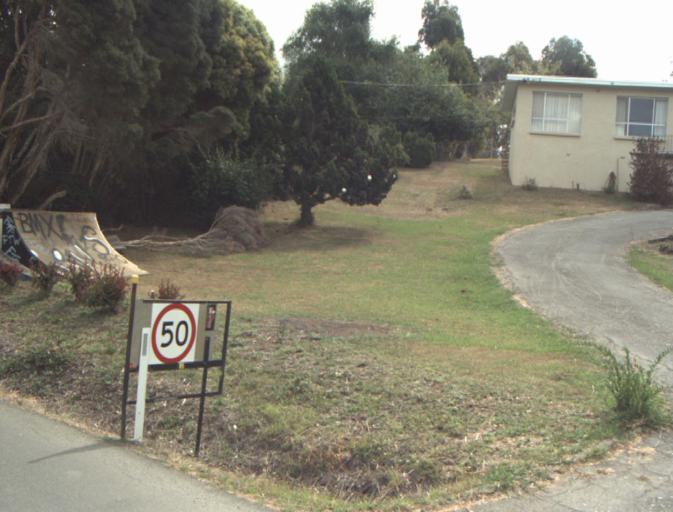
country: AU
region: Tasmania
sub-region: Launceston
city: Mayfield
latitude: -41.3152
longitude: 147.0348
